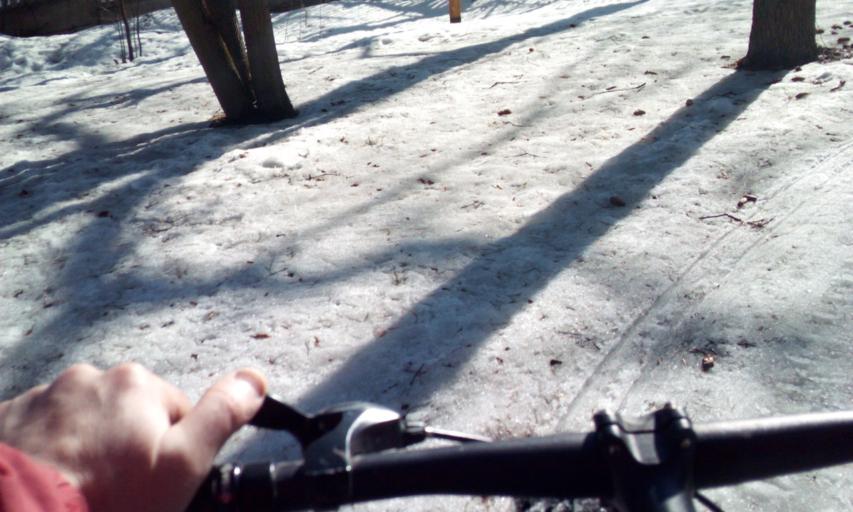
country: RU
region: Moscow
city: Novo-Peredelkino
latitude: 55.6629
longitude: 37.3466
